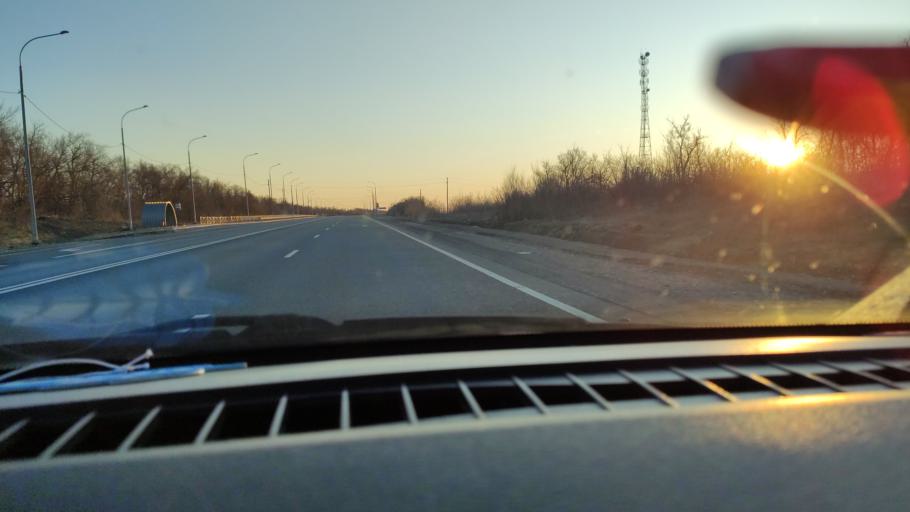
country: RU
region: Saratov
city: Yelshanka
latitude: 51.8923
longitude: 46.5257
